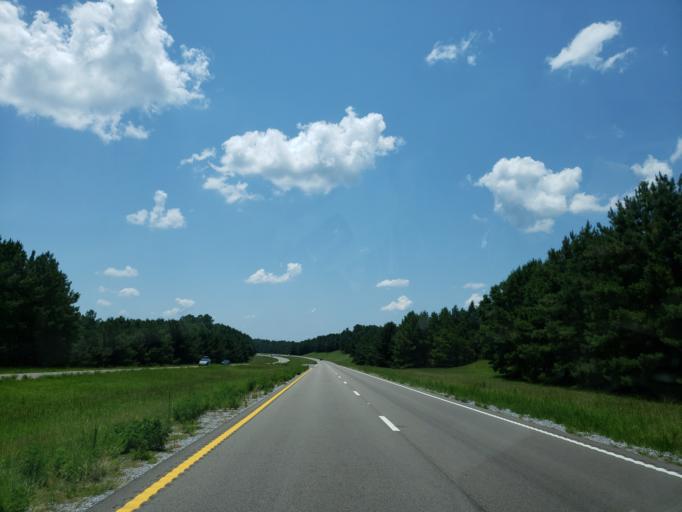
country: US
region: Mississippi
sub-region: Clarke County
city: Stonewall
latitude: 32.2058
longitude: -88.7024
